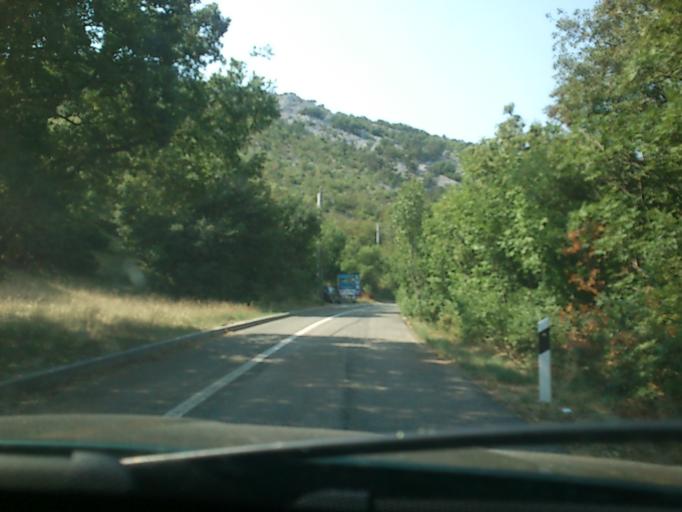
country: HR
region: Primorsko-Goranska
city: Banjol
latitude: 44.7051
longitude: 14.9022
